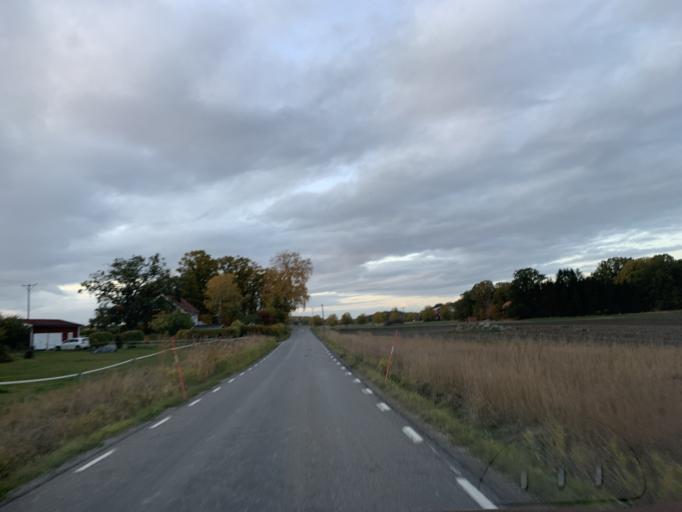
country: SE
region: Stockholm
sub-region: Nynashamns Kommun
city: Osmo
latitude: 58.9024
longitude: 17.7909
